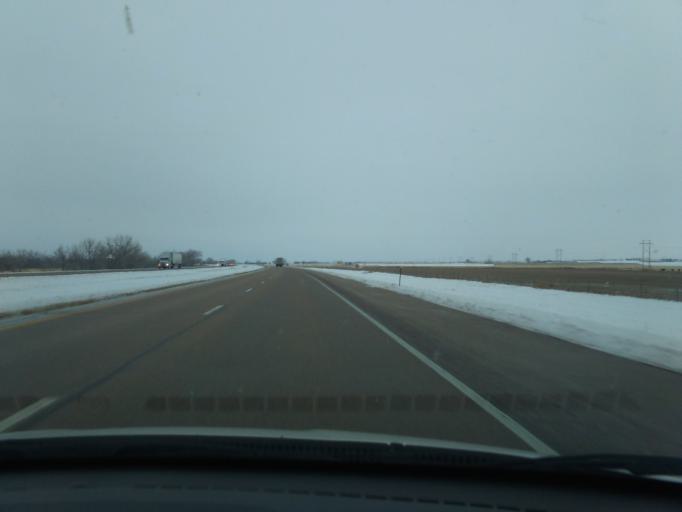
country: US
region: Nebraska
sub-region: Keith County
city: Ogallala
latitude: 41.0992
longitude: -101.7842
